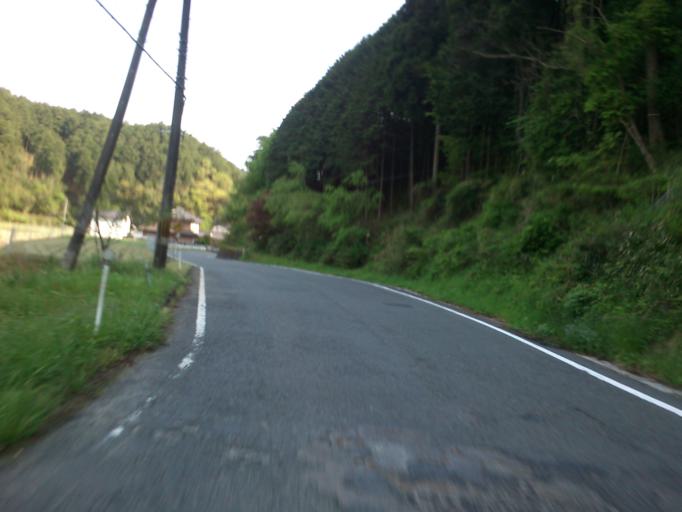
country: JP
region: Kyoto
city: Fukuchiyama
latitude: 35.3260
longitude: 135.0058
